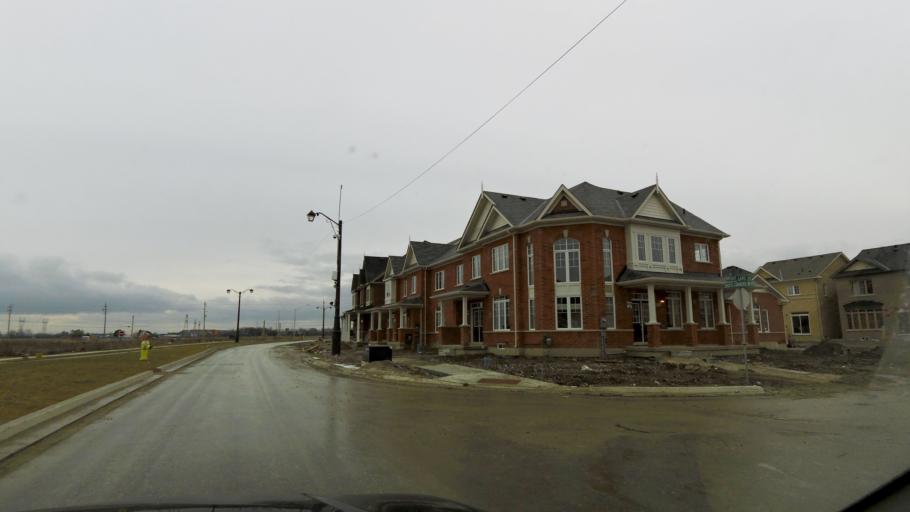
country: CA
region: Ontario
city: Vaughan
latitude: 43.8307
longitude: -79.6594
